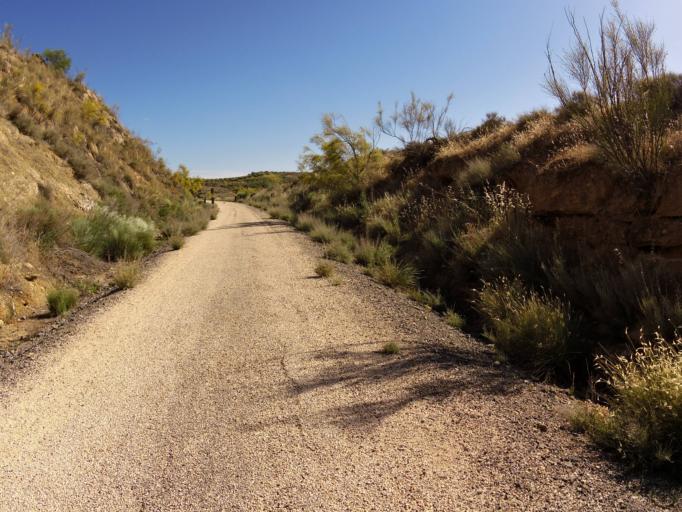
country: ES
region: Andalusia
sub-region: Provincia de Jaen
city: Alcaudete
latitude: 37.5955
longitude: -4.1561
